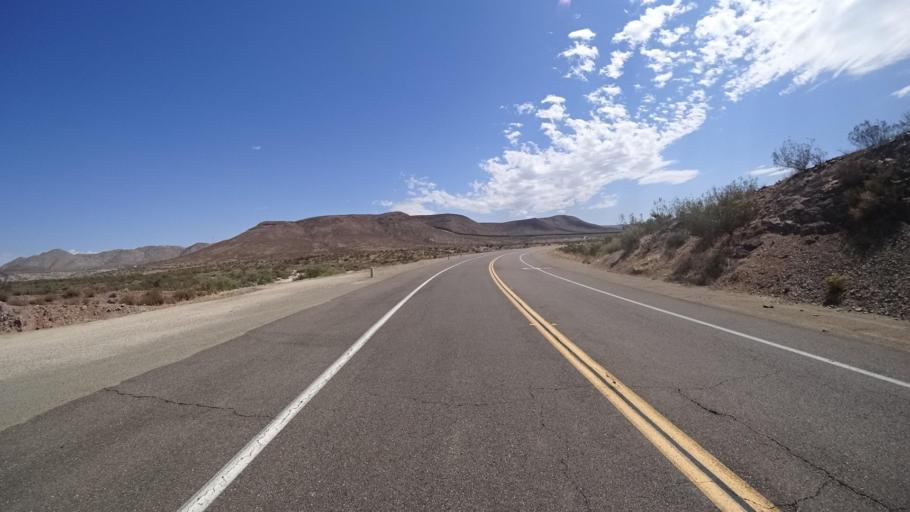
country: MX
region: Baja California
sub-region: Tecate
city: Cereso del Hongo
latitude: 32.6257
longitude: -116.1599
